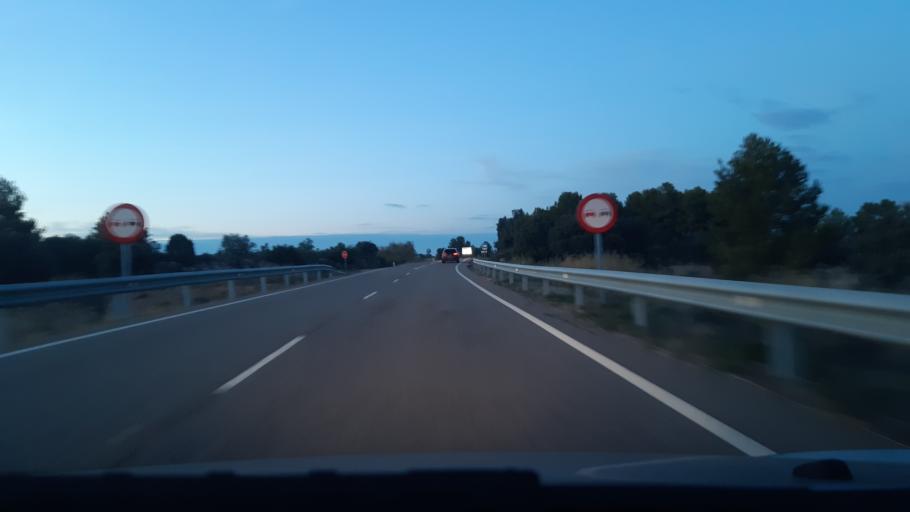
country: ES
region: Aragon
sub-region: Provincia de Teruel
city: Calaceite
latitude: 40.9745
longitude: 0.2041
